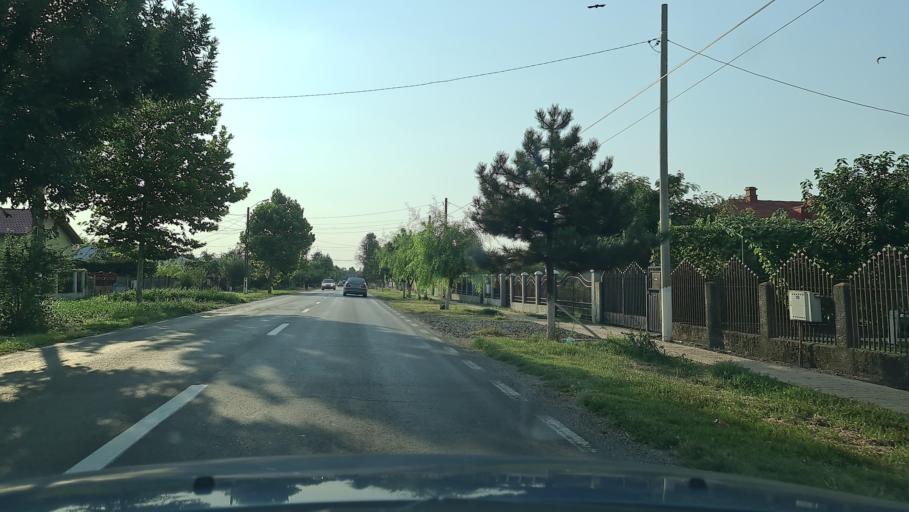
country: RO
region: Calarasi
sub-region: Comuna Dor Marunt
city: Dor Marunt
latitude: 44.4399
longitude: 26.9421
